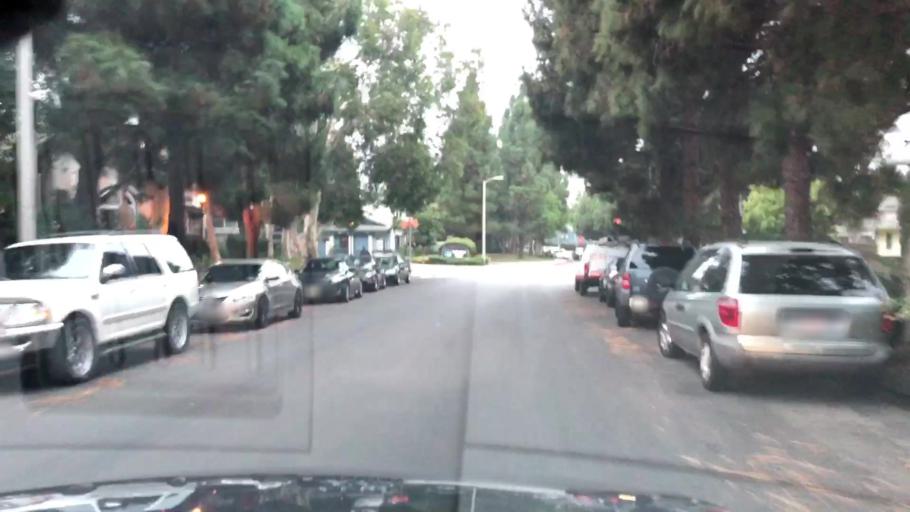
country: US
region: California
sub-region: Ventura County
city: Channel Islands Beach
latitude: 34.1809
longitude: -119.2147
